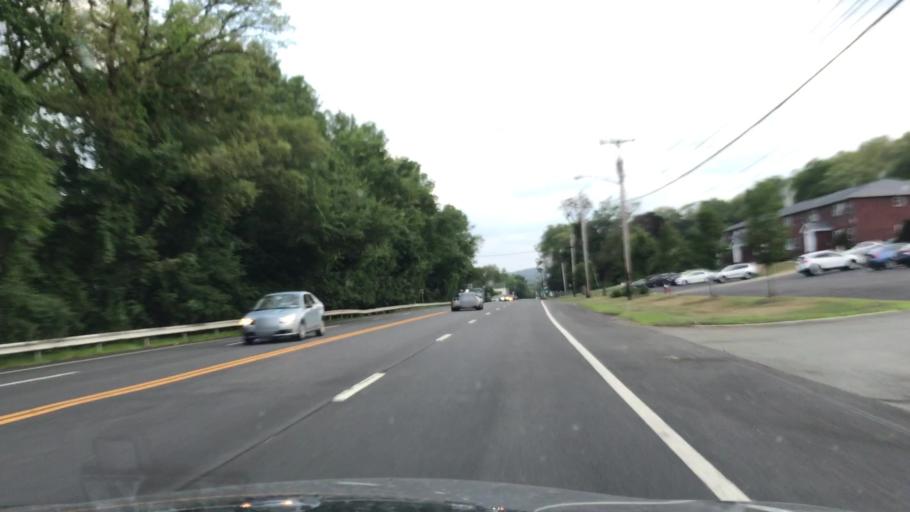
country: US
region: New York
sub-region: Rockland County
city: Sloatsburg
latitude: 41.1802
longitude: -74.1855
